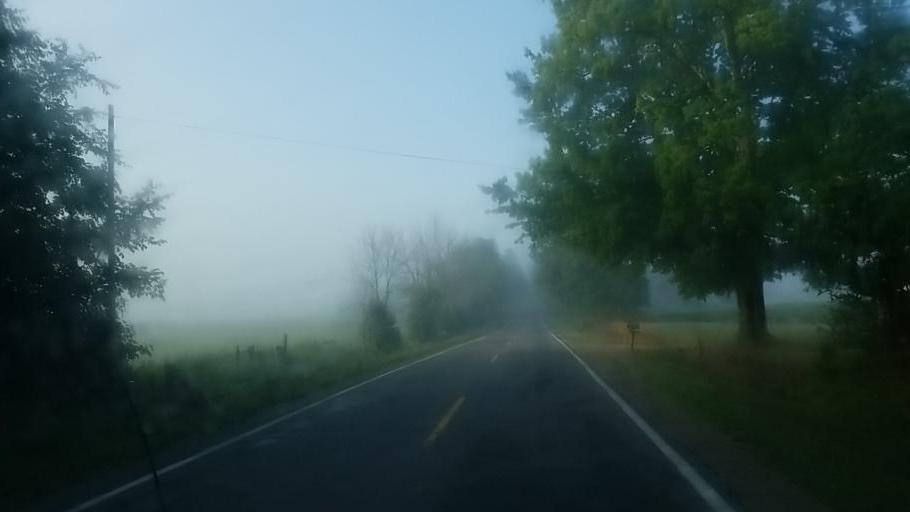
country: US
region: Michigan
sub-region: Muskegon County
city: Twin Lake
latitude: 43.4590
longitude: -86.0791
